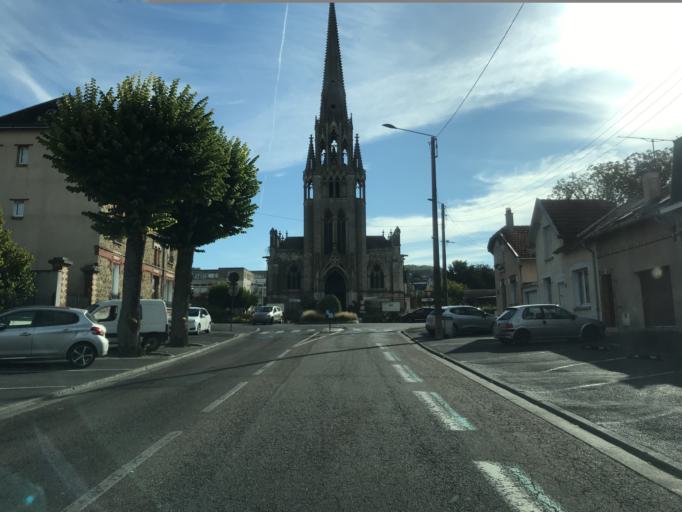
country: FR
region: Champagne-Ardenne
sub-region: Departement de la Marne
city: Pierry
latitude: 49.0322
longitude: 3.9525
